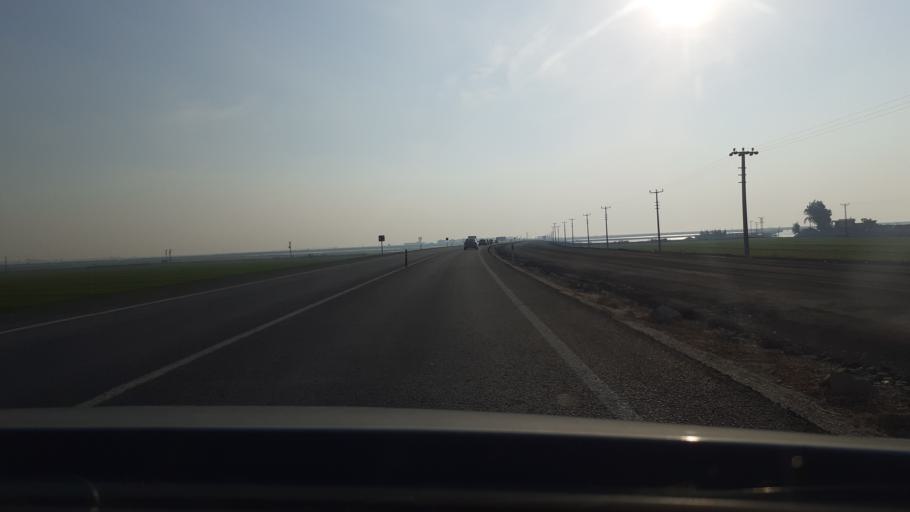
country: TR
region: Hatay
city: Serinyol
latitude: 36.3706
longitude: 36.2527
